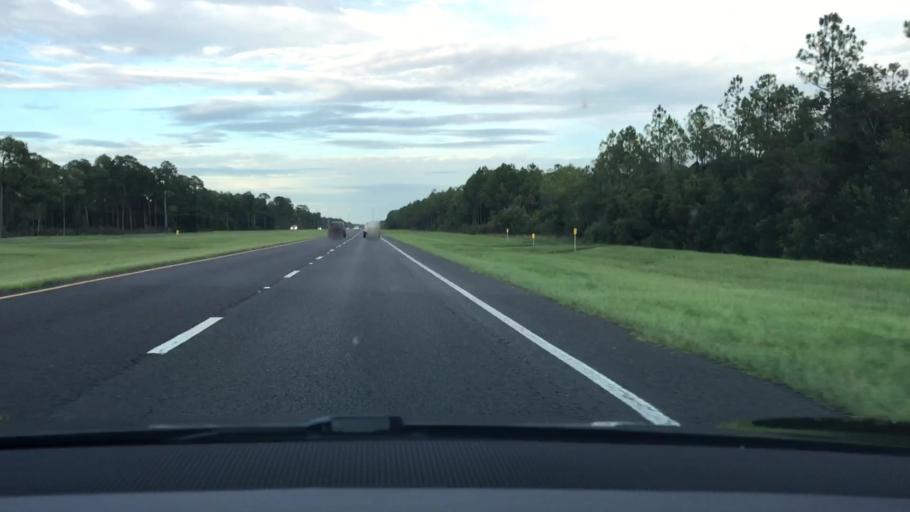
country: US
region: Florida
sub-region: Walton County
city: Seaside
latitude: 30.3569
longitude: -86.1419
